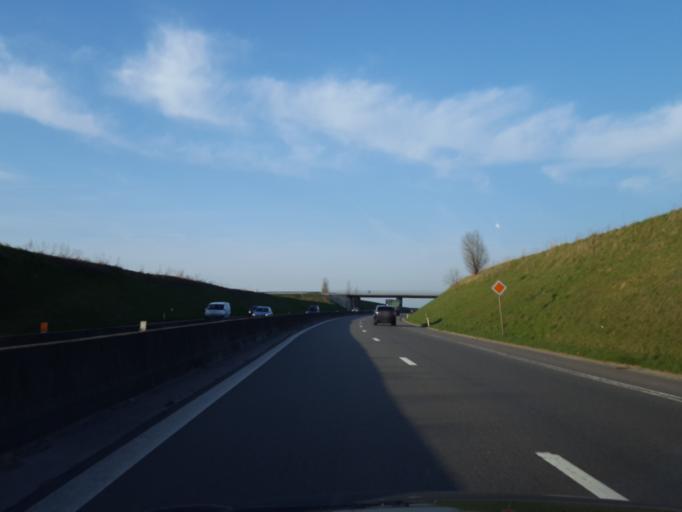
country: BE
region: Wallonia
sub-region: Province du Brabant Wallon
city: Nivelles
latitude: 50.5972
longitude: 4.3806
